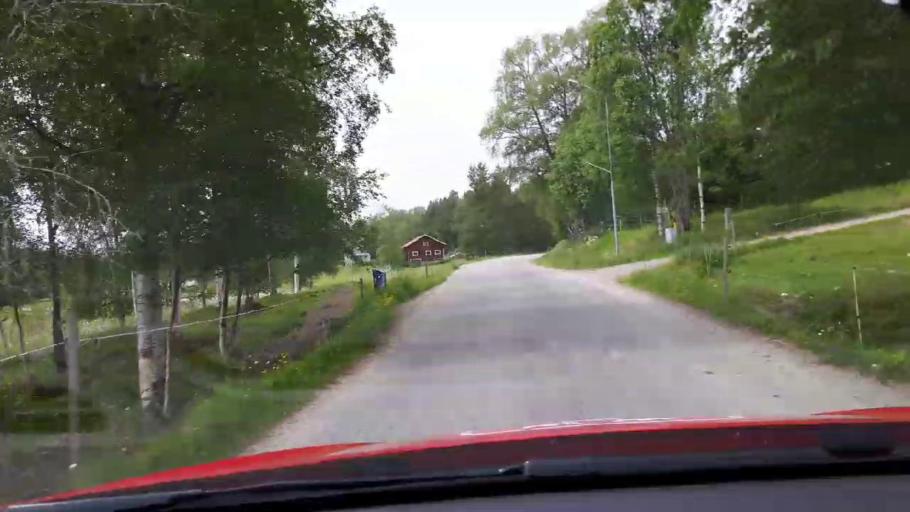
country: SE
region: Jaemtland
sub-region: Harjedalens Kommun
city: Sveg
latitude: 62.4114
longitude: 13.6673
